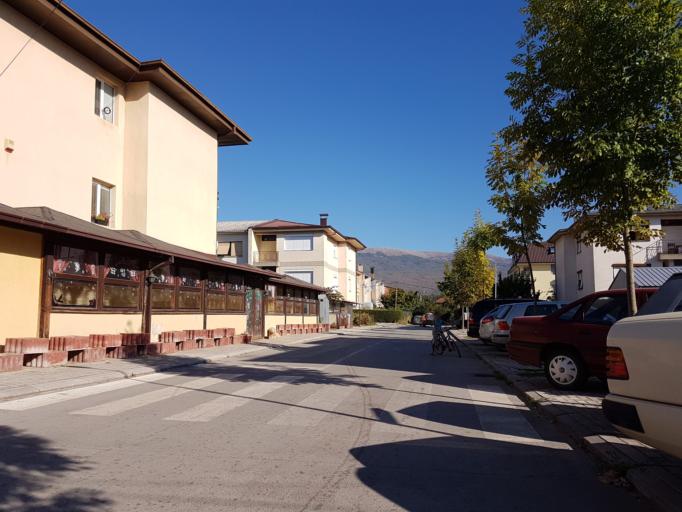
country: MK
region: Ohrid
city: Ohrid
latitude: 41.1230
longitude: 20.7811
